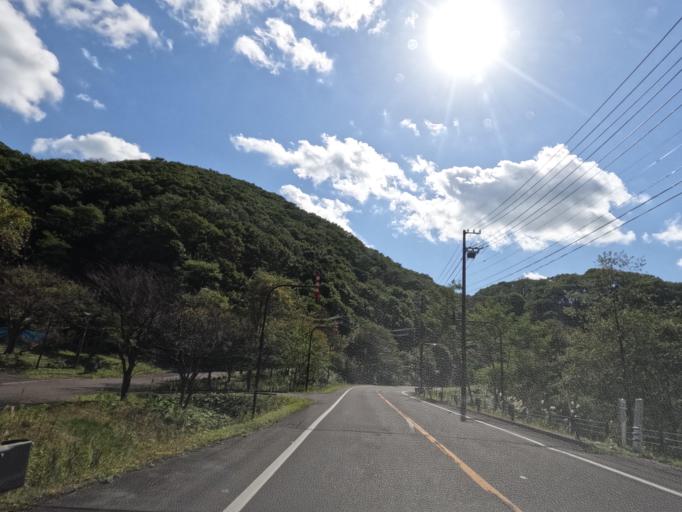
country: JP
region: Hokkaido
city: Shiraoi
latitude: 42.4837
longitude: 141.1455
